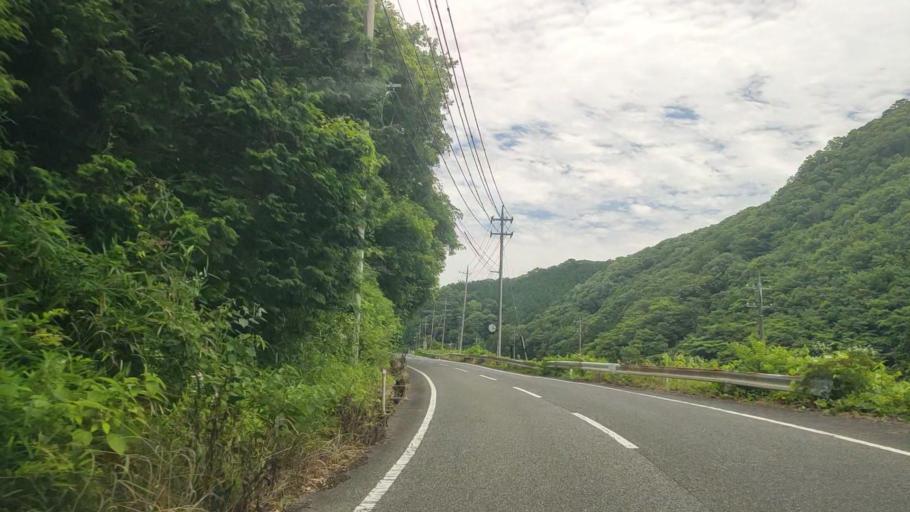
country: JP
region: Okayama
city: Tsuyama
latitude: 35.0662
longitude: 134.2284
